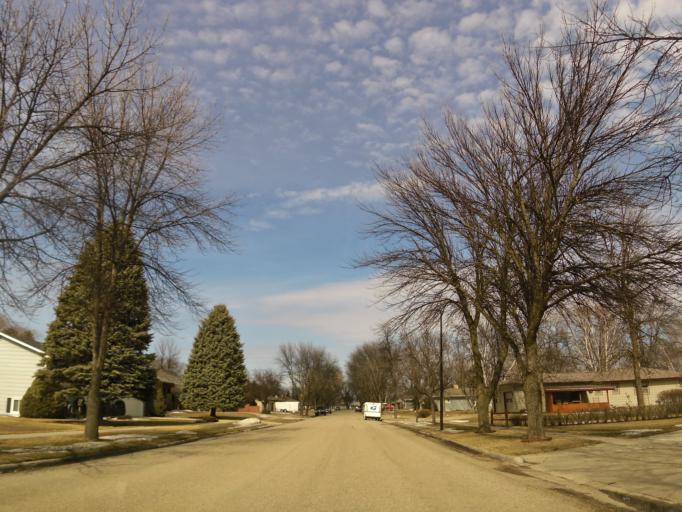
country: US
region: North Dakota
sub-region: Walsh County
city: Grafton
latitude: 48.4083
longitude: -97.4204
